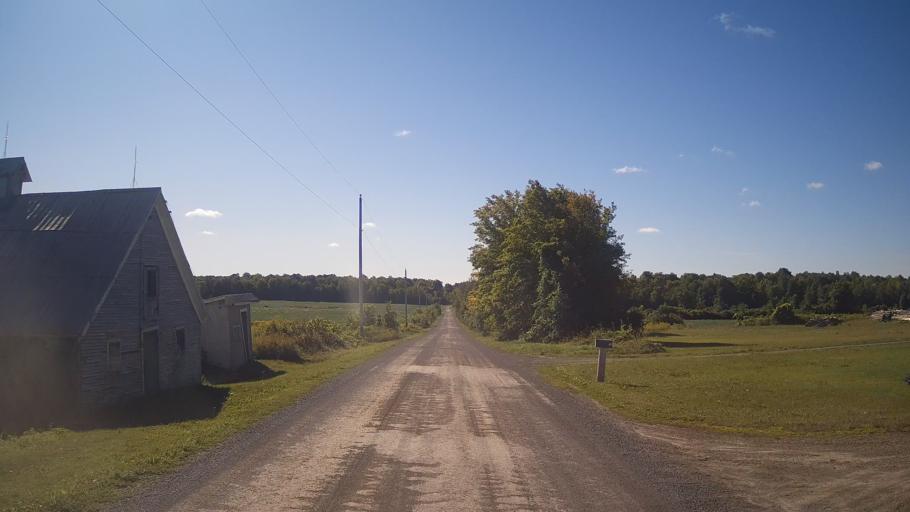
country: CA
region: Ontario
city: Prescott
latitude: 44.9742
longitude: -75.5704
